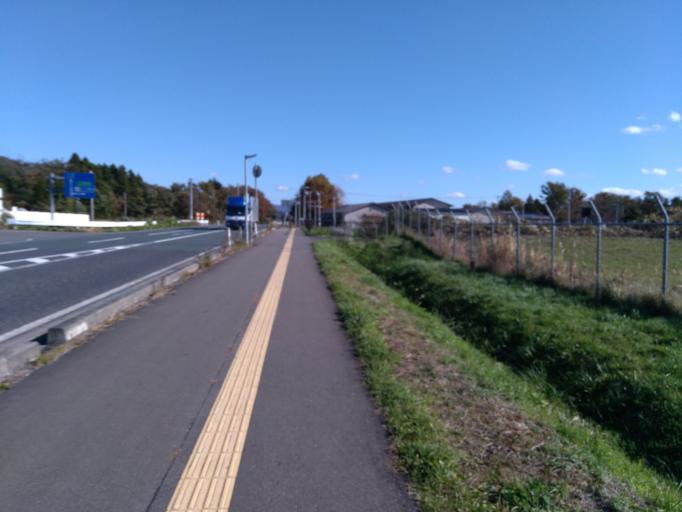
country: JP
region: Iwate
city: Hanamaki
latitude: 39.4416
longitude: 141.1397
